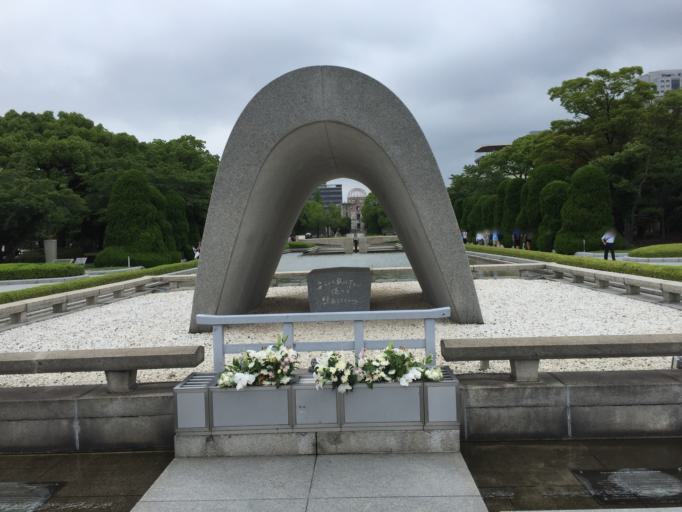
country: JP
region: Hiroshima
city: Hiroshima-shi
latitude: 34.3929
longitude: 132.4525
